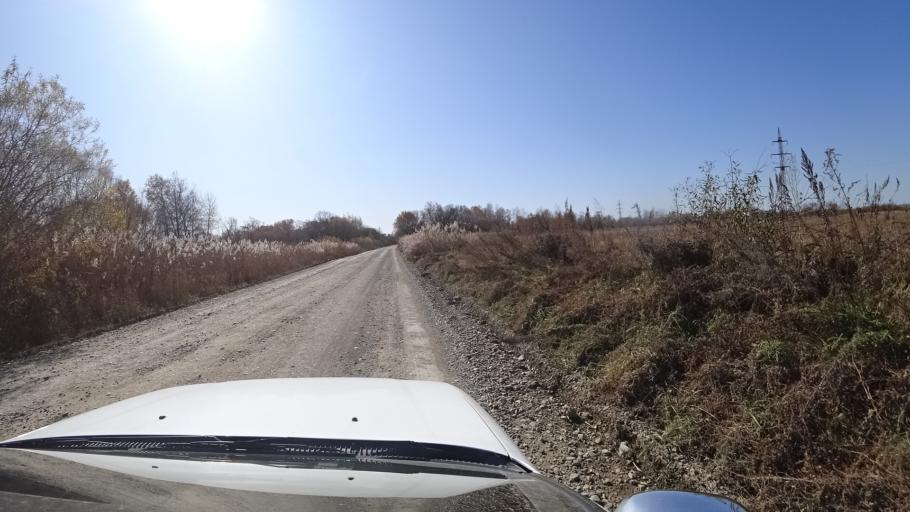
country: RU
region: Primorskiy
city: Dal'nerechensk
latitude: 45.9216
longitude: 133.7781
